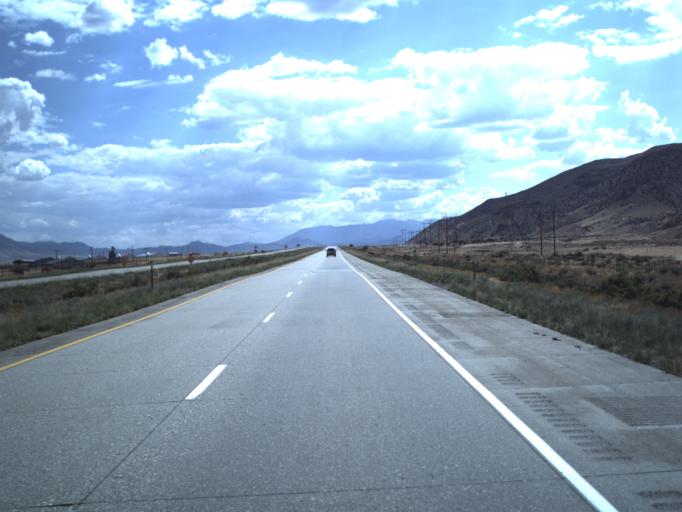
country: US
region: Utah
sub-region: Sevier County
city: Richfield
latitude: 38.7213
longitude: -112.1320
